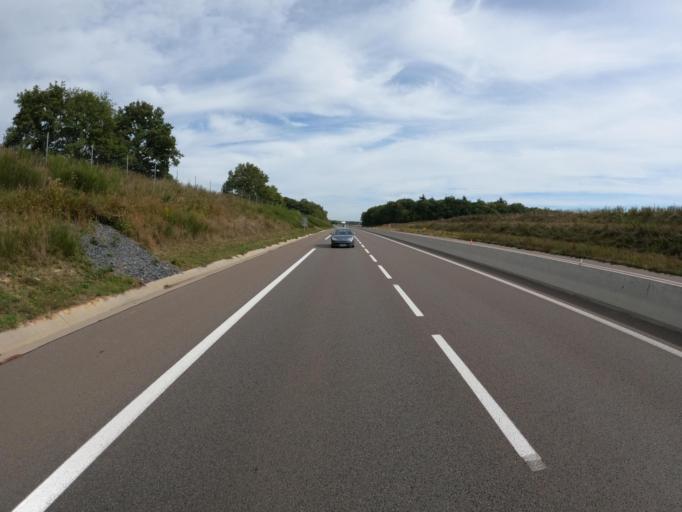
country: FR
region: Bourgogne
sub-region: Departement de Saone-et-Loire
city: Genelard
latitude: 46.5965
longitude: 4.2377
